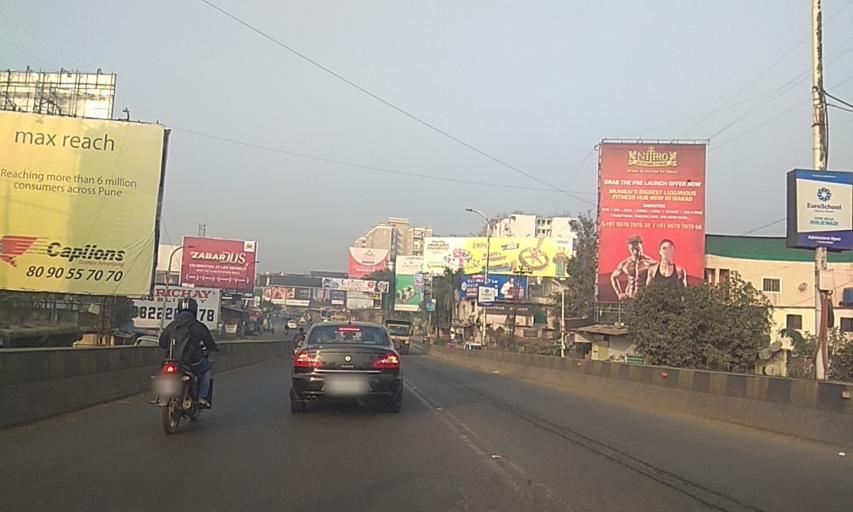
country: IN
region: Maharashtra
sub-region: Pune Division
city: Pimpri
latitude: 18.5920
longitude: 73.7557
